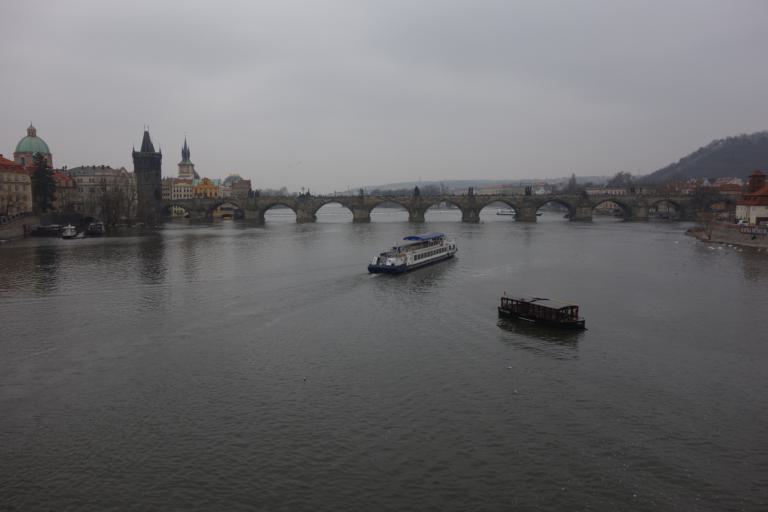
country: CZ
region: Praha
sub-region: Praha 1
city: Stare Mesto
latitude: 50.0895
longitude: 14.4128
